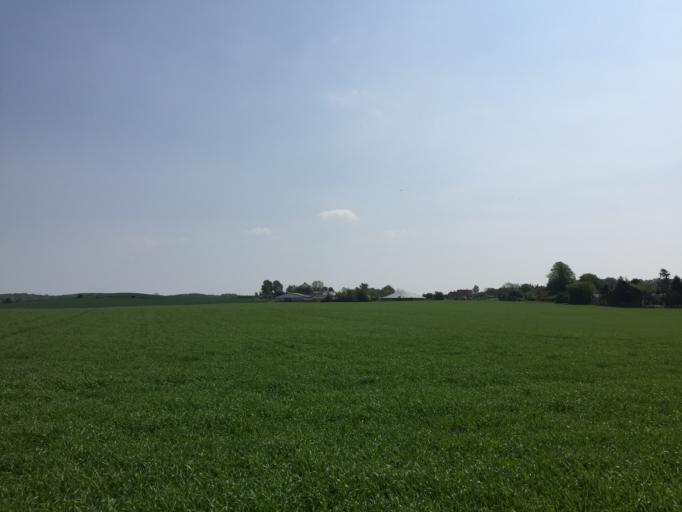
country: DK
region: South Denmark
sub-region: Langeland Kommune
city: Rudkobing
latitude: 54.9795
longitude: 10.8079
